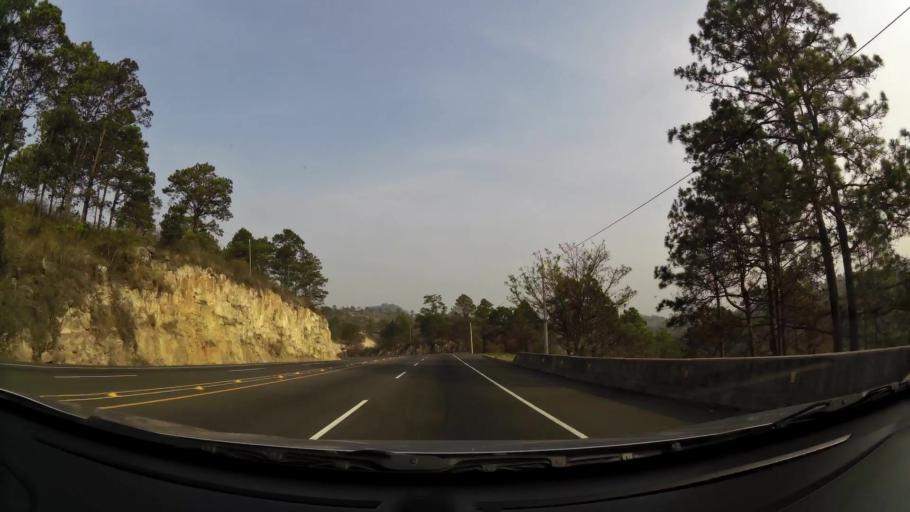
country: HN
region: Francisco Morazan
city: Zambrano
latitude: 14.2555
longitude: -87.3867
